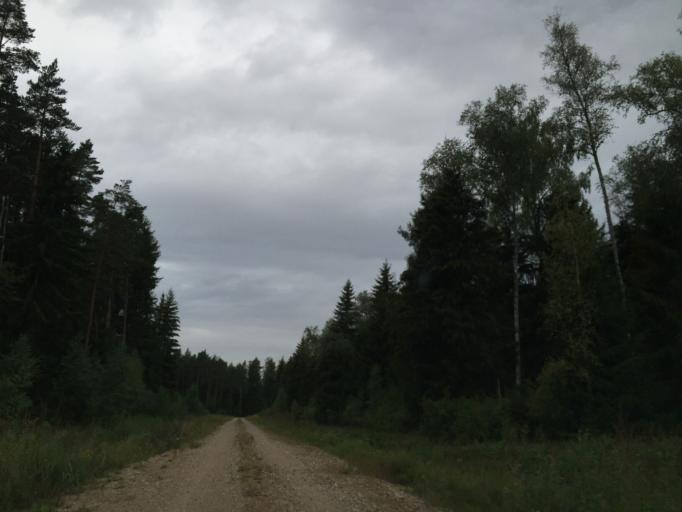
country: LV
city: Tireli
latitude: 56.8390
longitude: 23.6401
